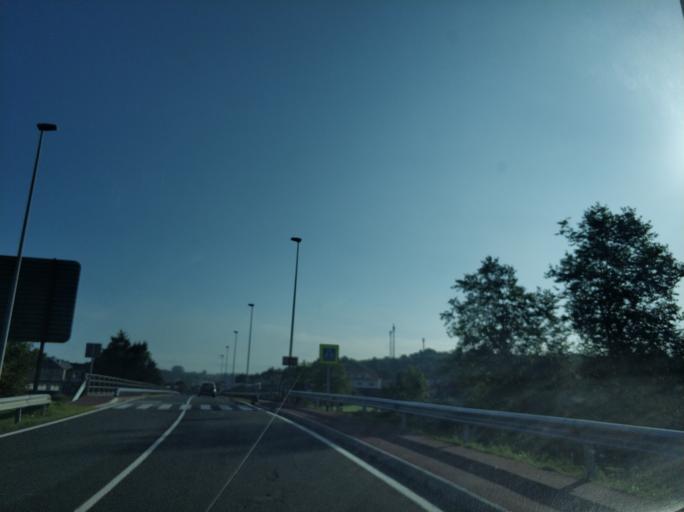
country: ES
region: Cantabria
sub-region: Provincia de Cantabria
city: Miengo
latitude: 43.4032
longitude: -3.9508
